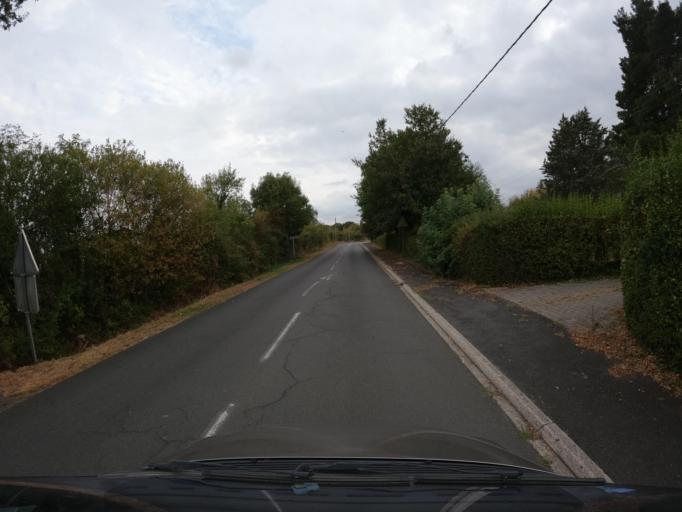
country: FR
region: Pays de la Loire
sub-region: Departement de Maine-et-Loire
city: La Romagne
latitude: 47.0575
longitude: -1.0259
